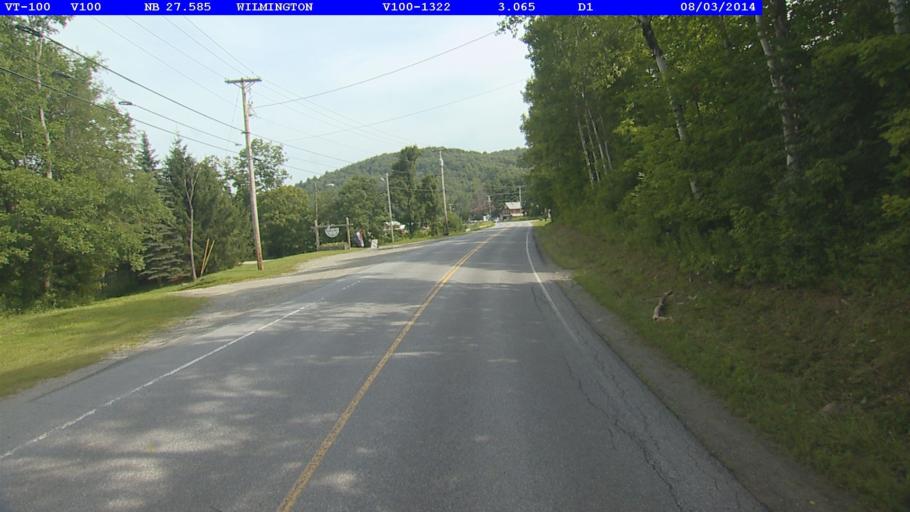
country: US
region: Vermont
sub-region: Windham County
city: Dover
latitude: 42.8741
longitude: -72.8630
